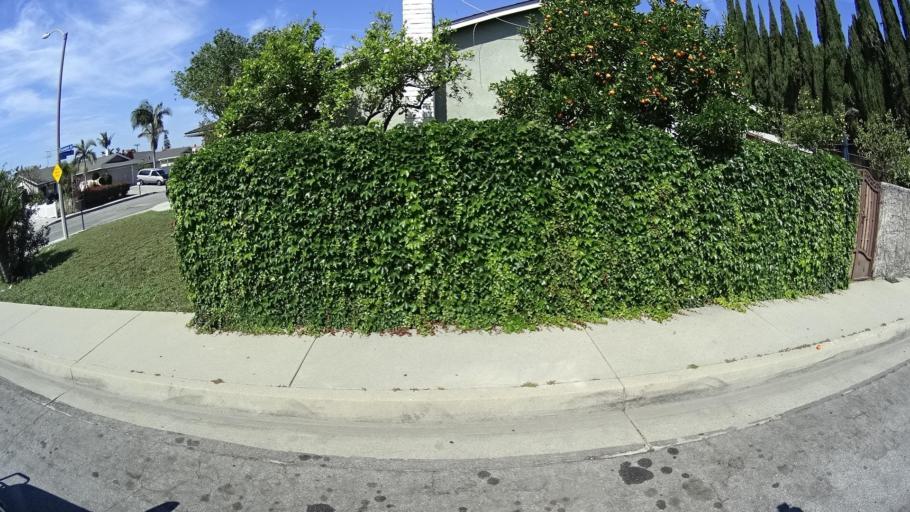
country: US
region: California
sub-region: Los Angeles County
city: South San Jose Hills
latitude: 34.0080
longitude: -117.8895
